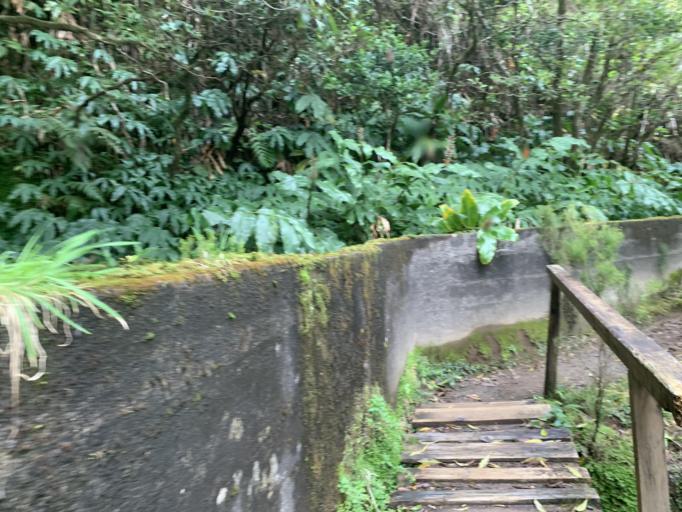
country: PT
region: Azores
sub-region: Vila Franca do Campo
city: Vila Franca do Campo
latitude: 37.7477
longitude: -25.4757
